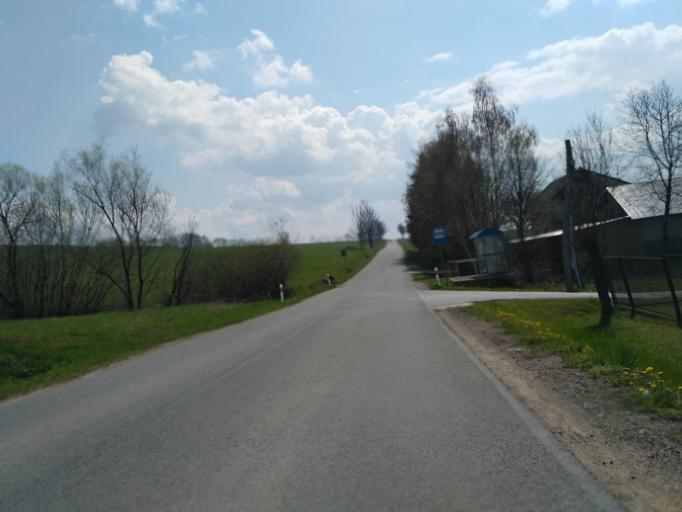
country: PL
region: Subcarpathian Voivodeship
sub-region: Powiat sanocki
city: Bukowsko
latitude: 49.4988
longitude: 22.0387
